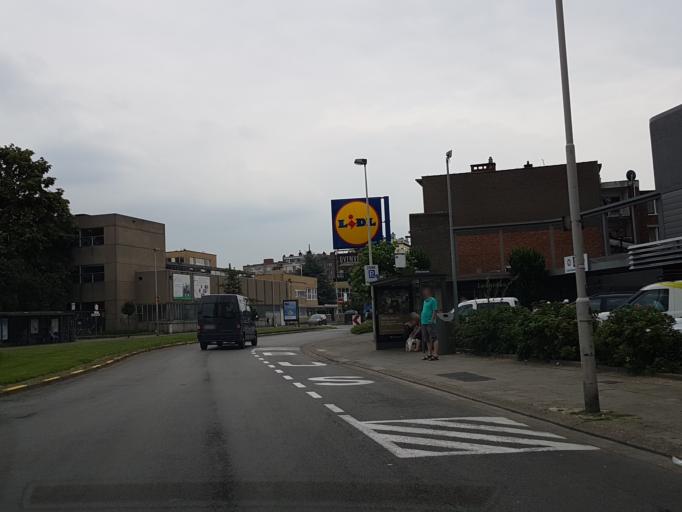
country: BE
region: Flanders
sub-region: Provincie Antwerpen
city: Borsbeek
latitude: 51.2226
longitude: 4.4589
